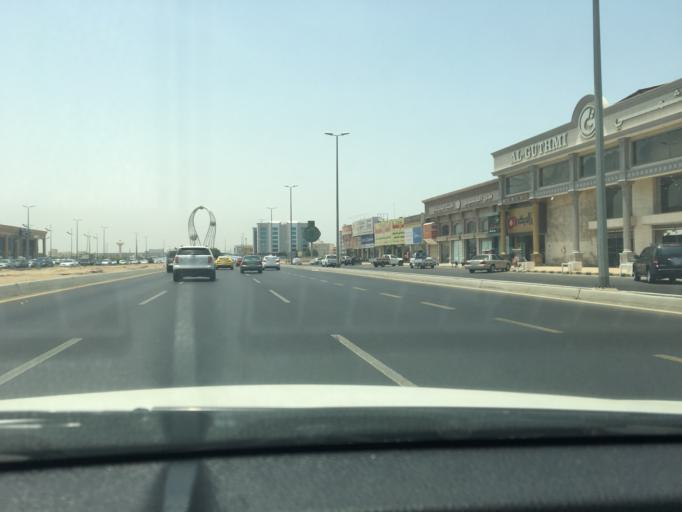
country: SA
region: Makkah
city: Jeddah
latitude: 21.5878
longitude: 39.1758
